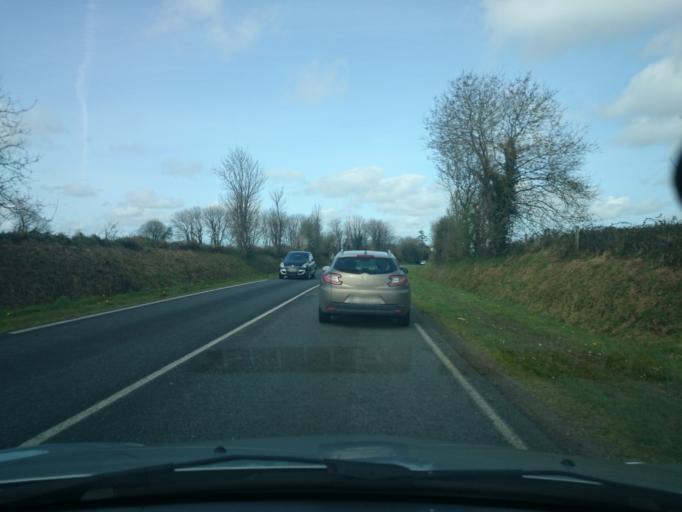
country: FR
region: Brittany
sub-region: Departement du Finistere
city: Gouesnou
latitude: 48.4416
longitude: -4.4518
